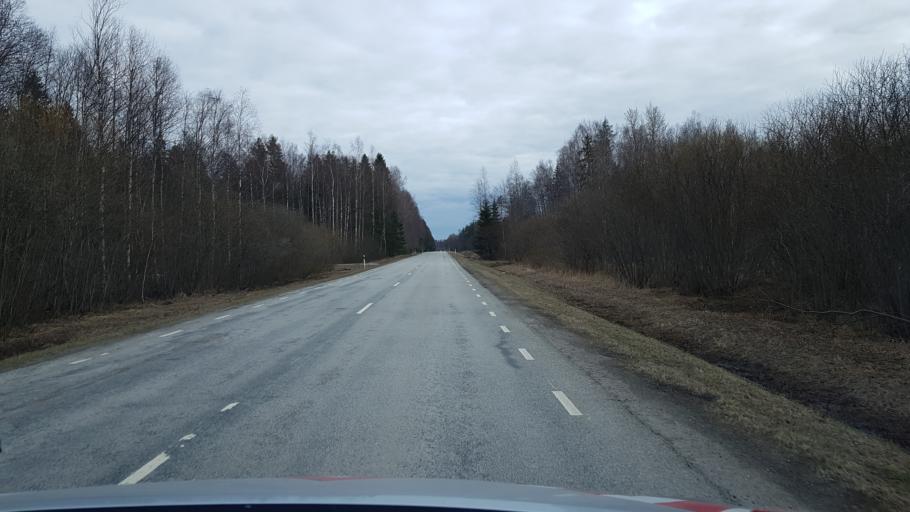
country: EE
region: Ida-Virumaa
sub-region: Toila vald
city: Toila
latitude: 59.3864
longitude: 27.5050
